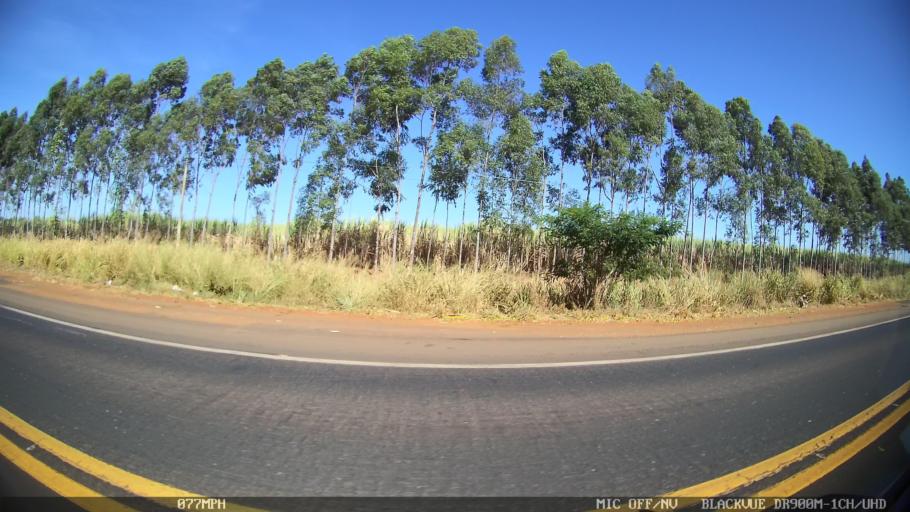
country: BR
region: Sao Paulo
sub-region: Olimpia
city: Olimpia
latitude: -20.6232
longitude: -48.7740
